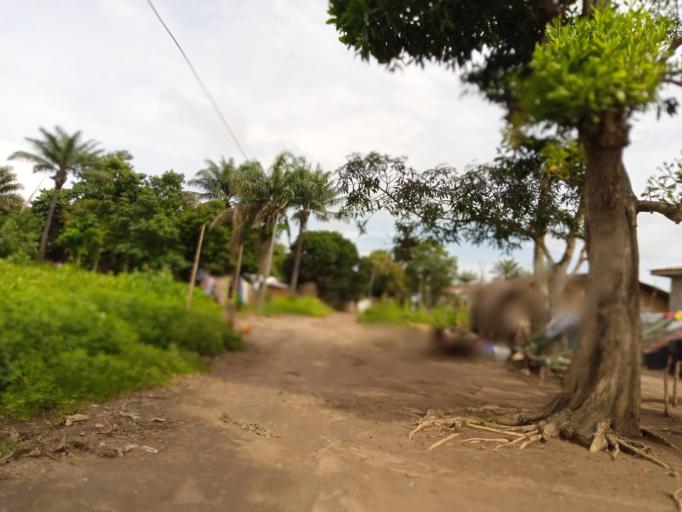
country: SL
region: Northern Province
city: Masoyila
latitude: 8.5919
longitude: -13.1960
